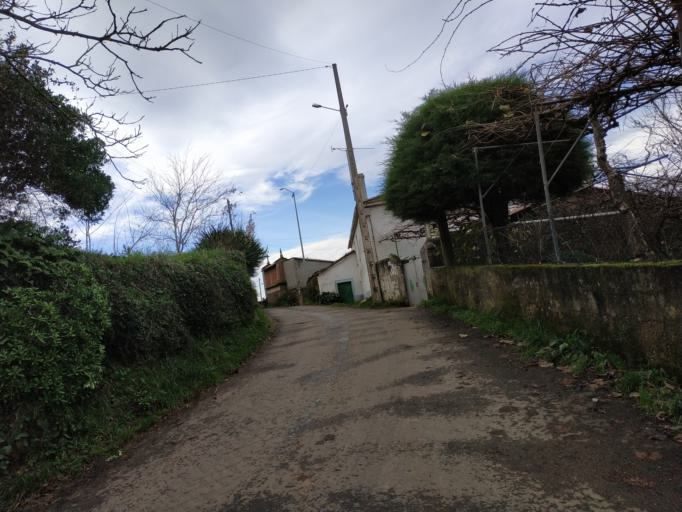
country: ES
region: Galicia
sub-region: Provincia de Pontevedra
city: Silleda
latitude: 42.7781
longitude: -8.1687
